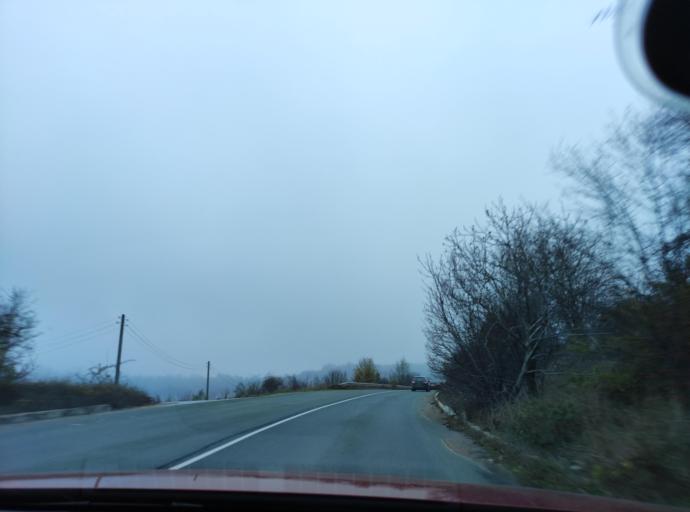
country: BG
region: Lovech
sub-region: Obshtina Yablanitsa
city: Yablanitsa
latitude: 43.0261
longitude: 24.0967
